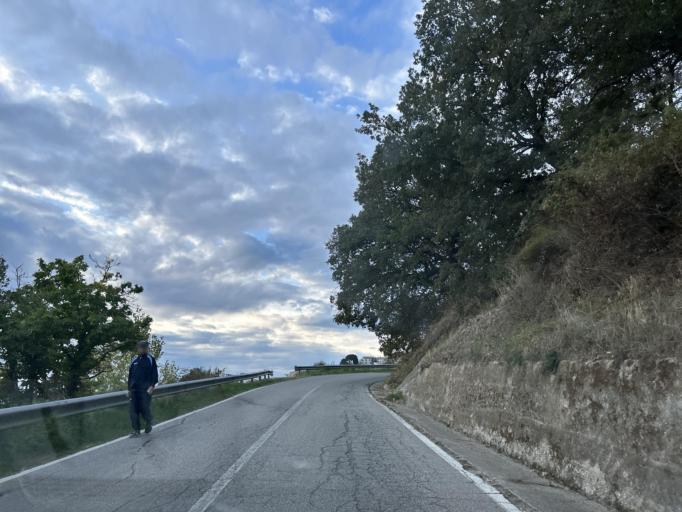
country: IT
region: Calabria
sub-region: Provincia di Catanzaro
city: Montauro
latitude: 38.7462
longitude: 16.5088
